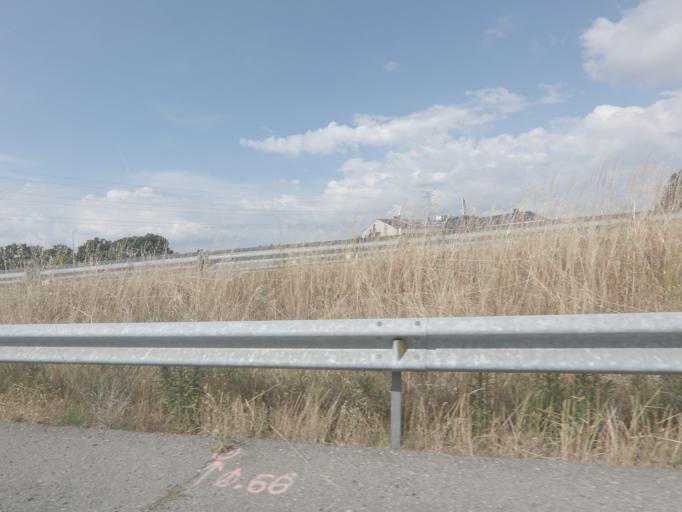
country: ES
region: Galicia
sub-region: Provincia de Ourense
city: Taboadela
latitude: 42.2505
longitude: -7.8657
